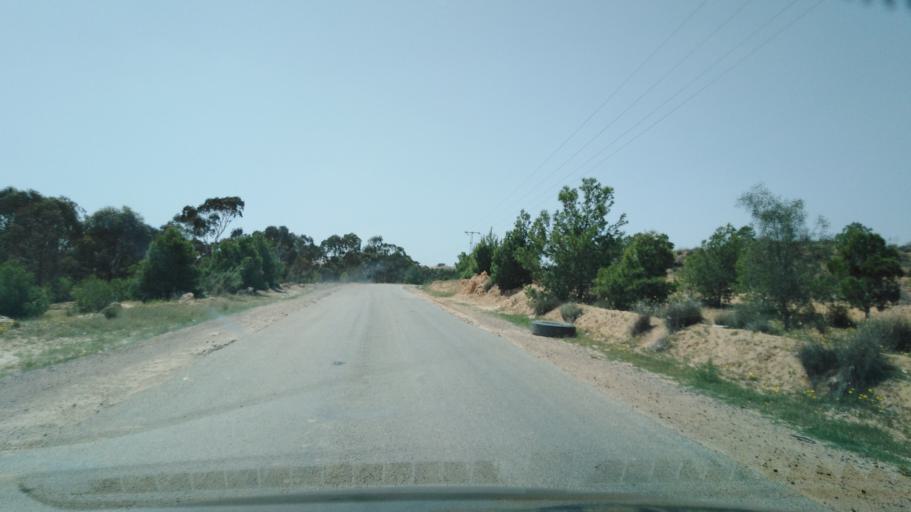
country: TN
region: Safaqis
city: Sfax
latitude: 34.7154
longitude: 10.5305
